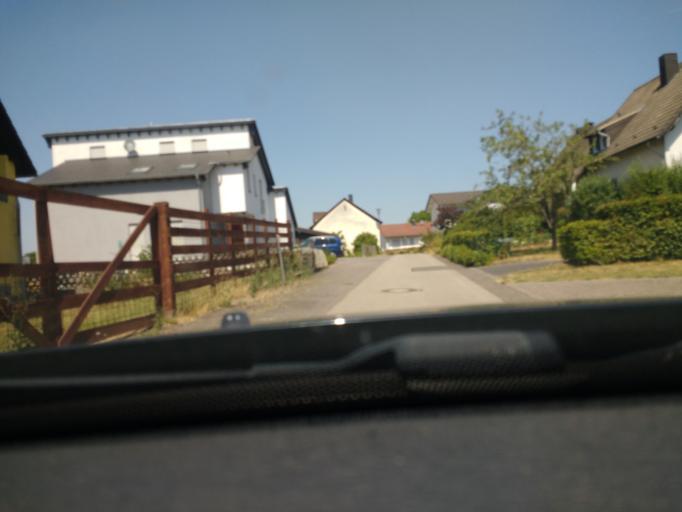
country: DE
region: Rheinland-Pfalz
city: Laufeld
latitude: 50.0786
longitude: 6.8666
